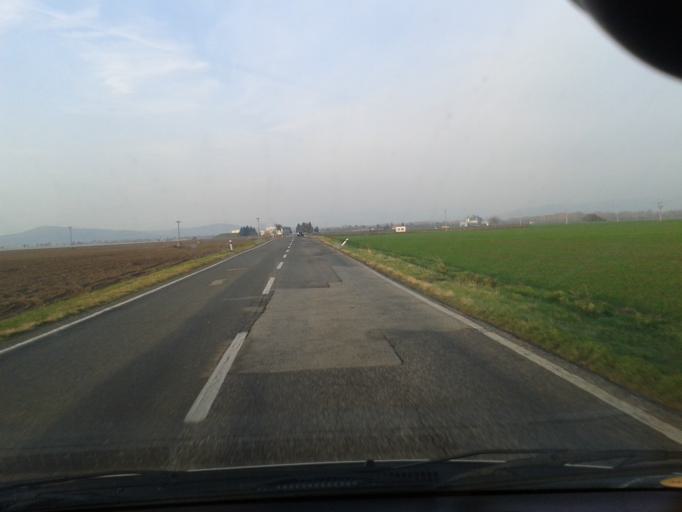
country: SK
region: Nitriansky
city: Tlmace
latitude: 48.2189
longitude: 18.5196
